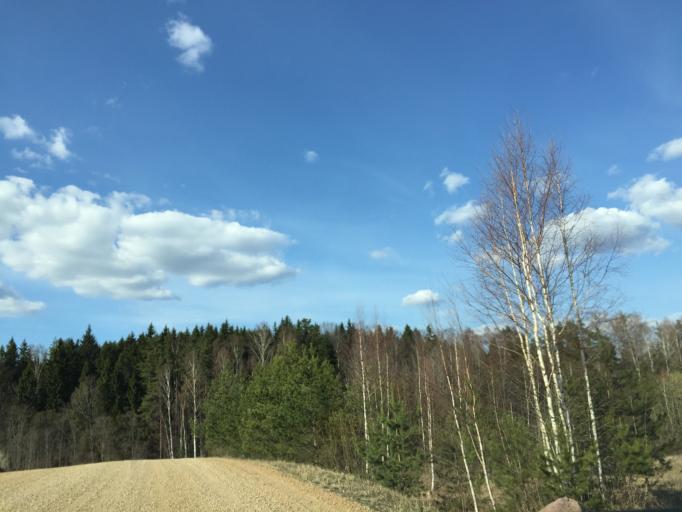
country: EE
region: Tartu
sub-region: Elva linn
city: Elva
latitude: 58.0975
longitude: 26.5084
